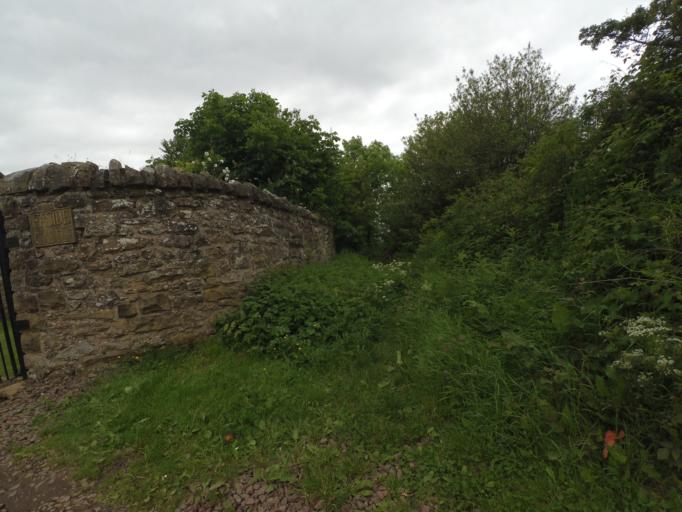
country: GB
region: Scotland
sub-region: East Lothian
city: Prestonpans
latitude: 55.9281
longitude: -2.9973
